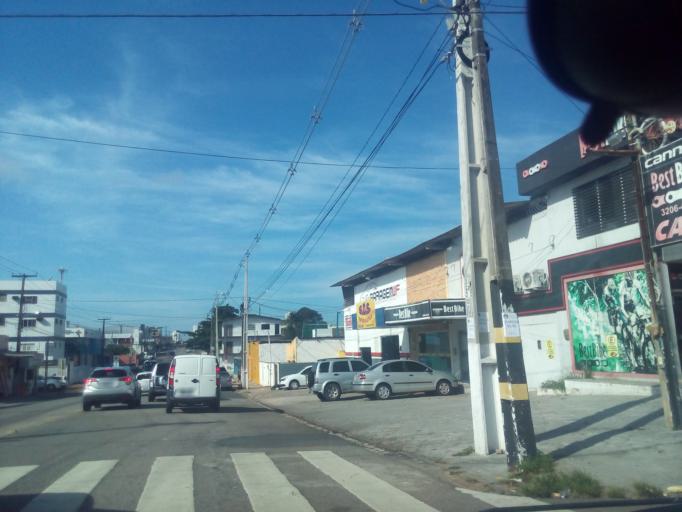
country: BR
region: Rio Grande do Norte
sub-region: Natal
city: Natal
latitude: -5.8129
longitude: -35.2127
